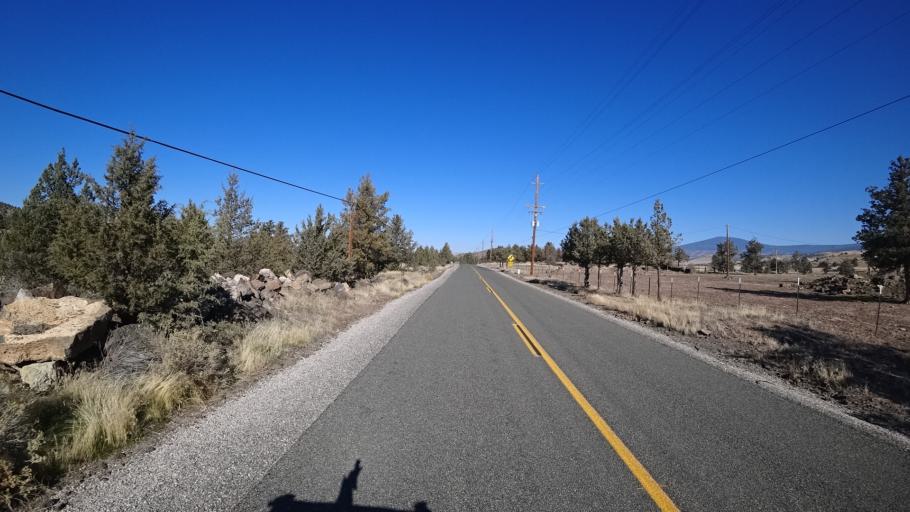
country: US
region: California
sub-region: Siskiyou County
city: Montague
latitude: 41.6694
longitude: -122.3697
